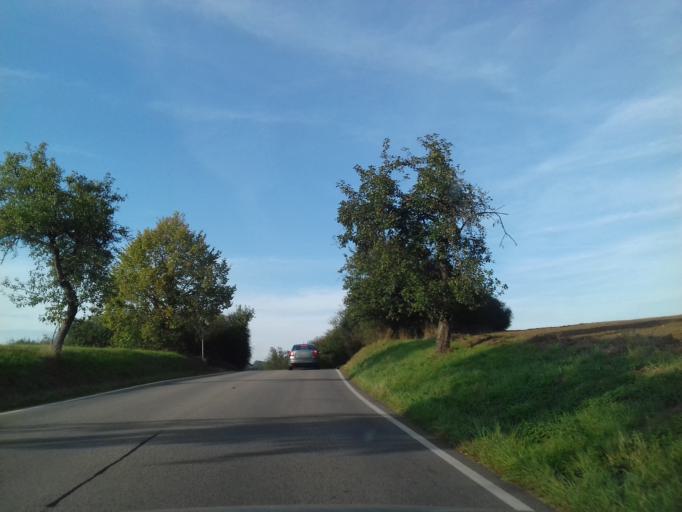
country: CZ
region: Central Bohemia
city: Kamenny Privoz
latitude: 49.8707
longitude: 14.5040
